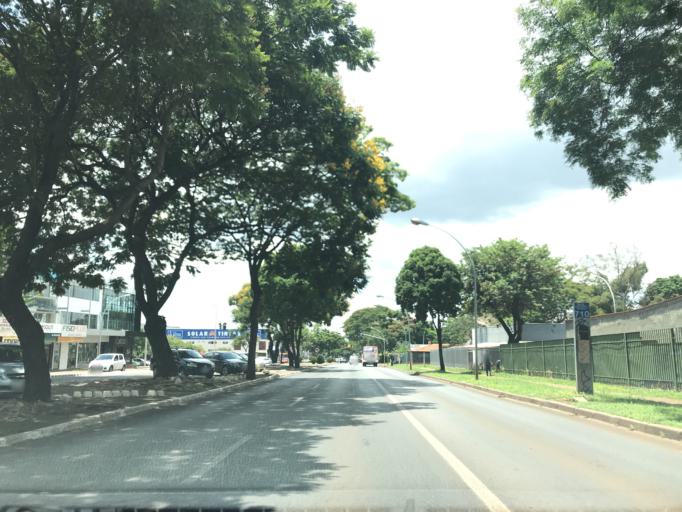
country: BR
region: Federal District
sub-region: Brasilia
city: Brasilia
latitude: -15.8148
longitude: -47.9097
